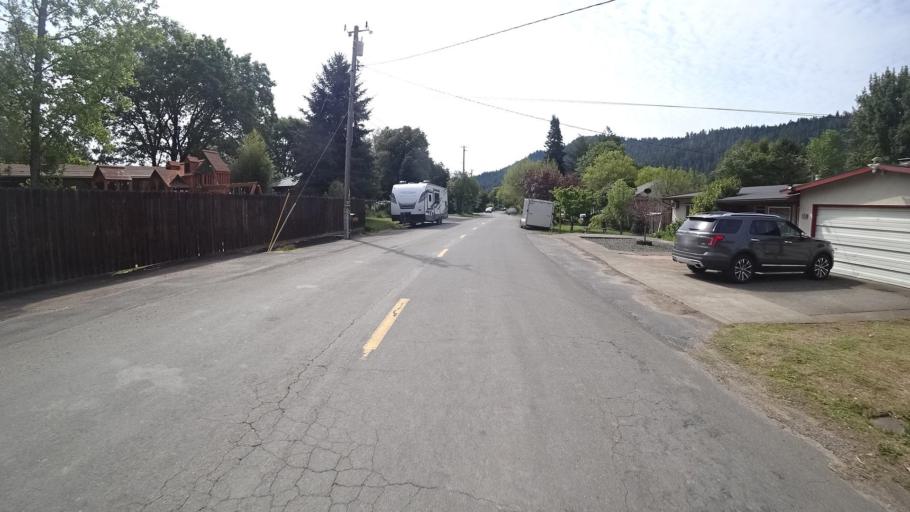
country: US
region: California
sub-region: Humboldt County
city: Redway
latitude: 40.1190
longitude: -123.8269
